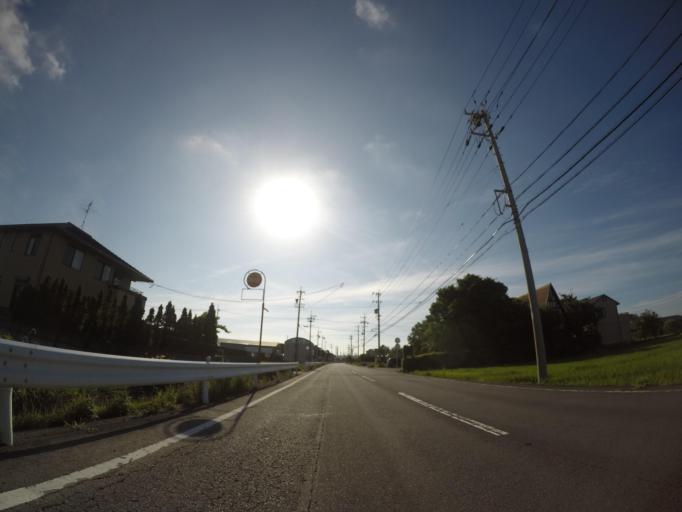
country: JP
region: Shizuoka
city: Yaizu
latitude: 34.8180
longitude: 138.3136
